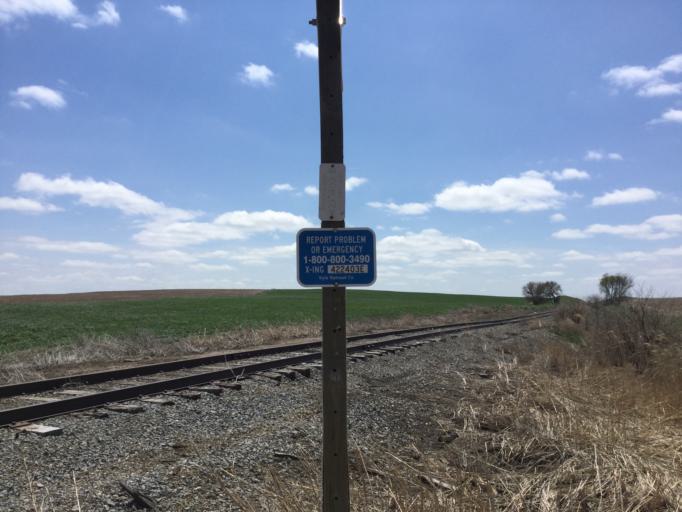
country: US
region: Kansas
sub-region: Osborne County
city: Osborne
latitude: 39.4663
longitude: -98.5919
